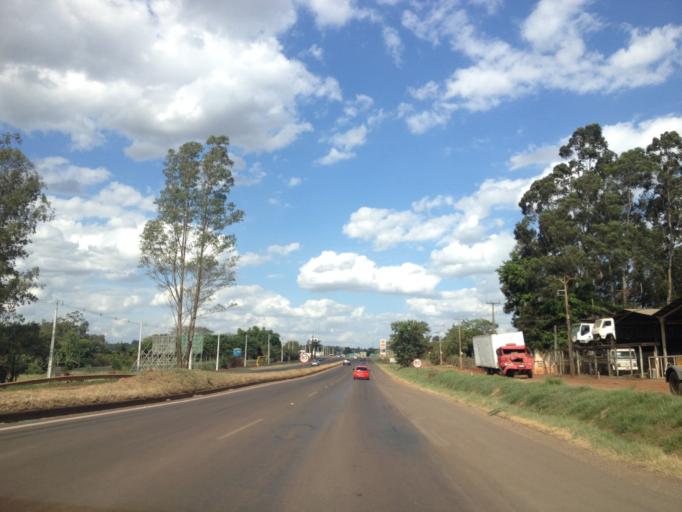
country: BR
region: Parana
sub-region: Sarandi
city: Sarandi
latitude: -23.4616
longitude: -51.8364
